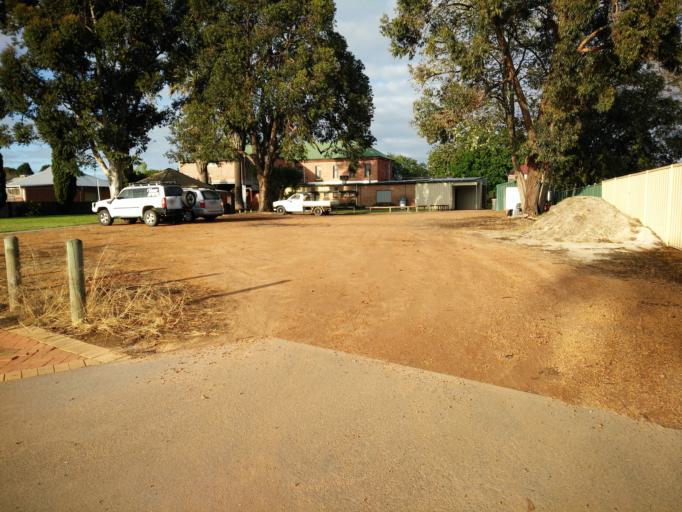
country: AU
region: Western Australia
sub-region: Donnybrook-Balingup
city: Donnybrook
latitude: -33.5724
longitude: 115.8250
